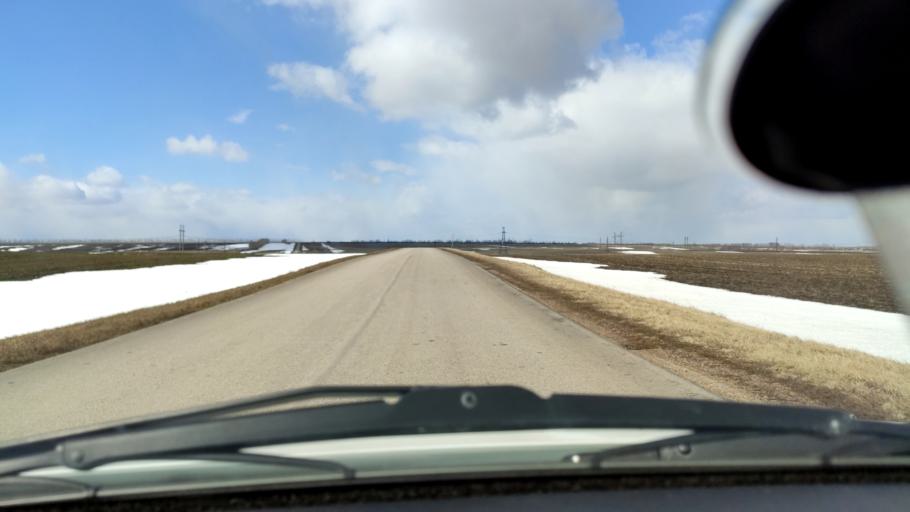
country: RU
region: Bashkortostan
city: Tolbazy
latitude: 54.1705
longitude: 55.9317
